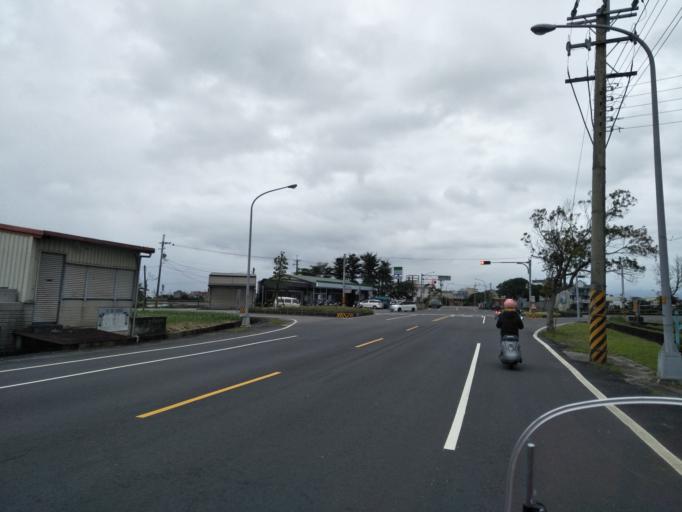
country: TW
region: Taiwan
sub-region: Yilan
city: Yilan
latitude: 24.7761
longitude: 121.7830
